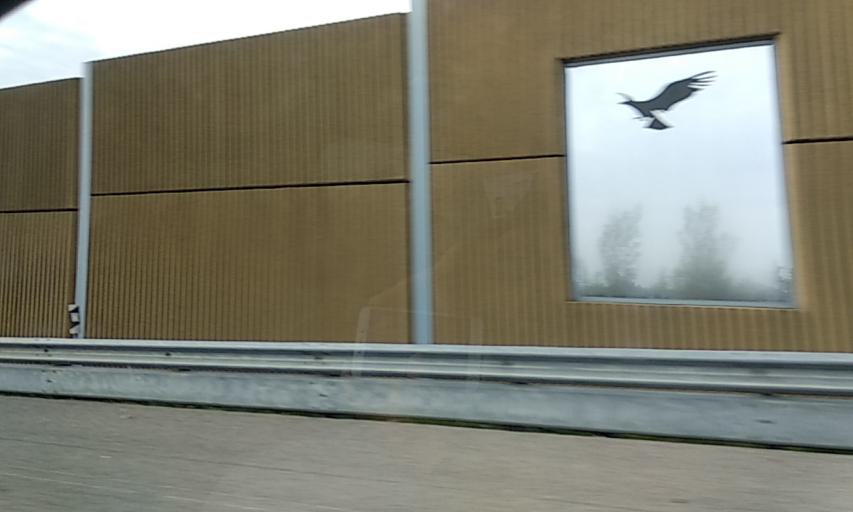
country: PT
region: Porto
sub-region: Trofa
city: Sao Romao do Coronado
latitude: 41.2801
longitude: -8.5613
